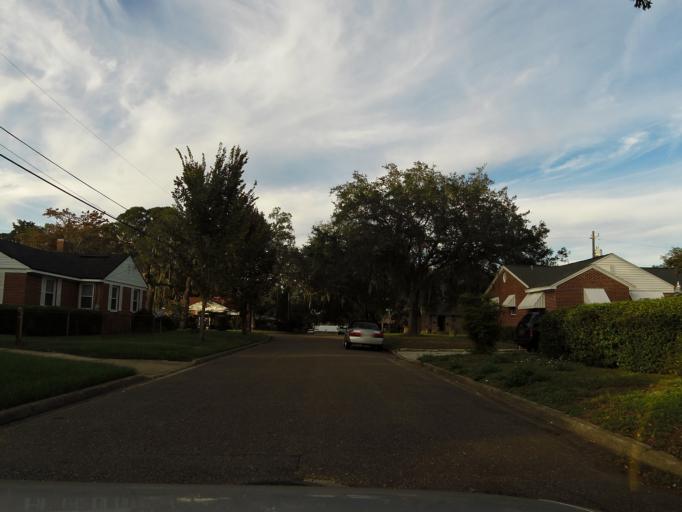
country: US
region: Florida
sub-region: Duval County
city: Jacksonville
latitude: 30.3891
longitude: -81.6589
